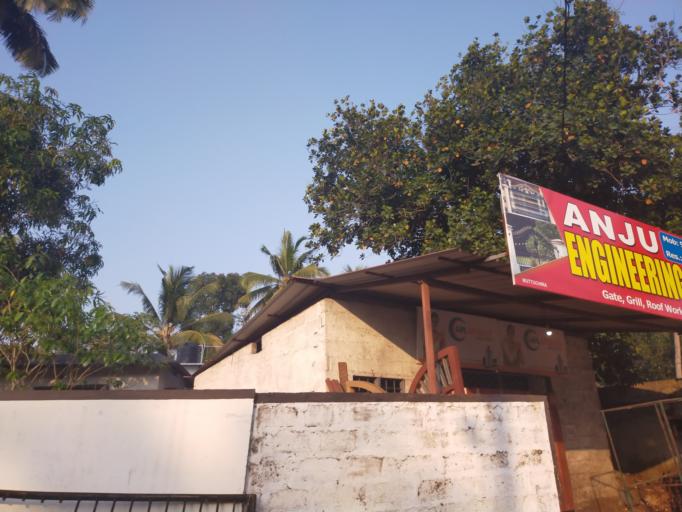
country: IN
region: Kerala
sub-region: Kottayam
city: Vaikam
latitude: 9.7560
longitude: 76.4981
